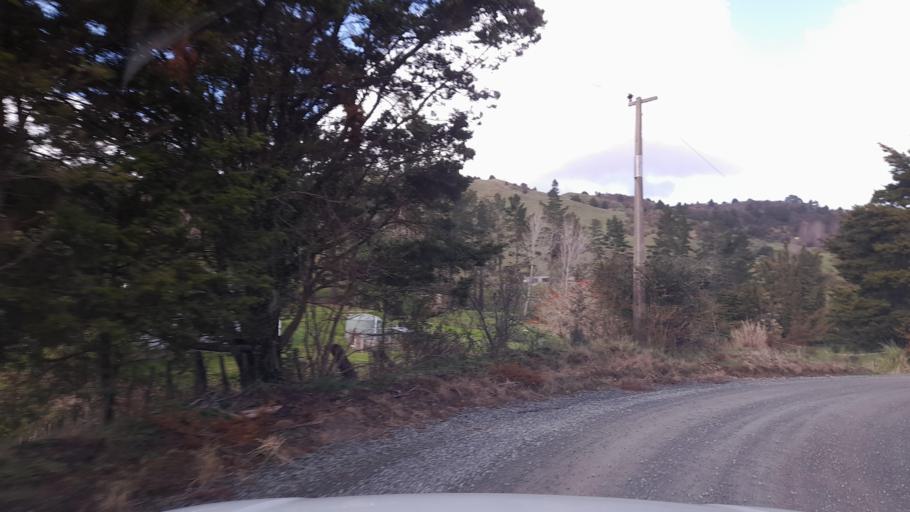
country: NZ
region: Northland
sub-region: Far North District
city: Kerikeri
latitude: -35.1303
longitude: 173.7400
